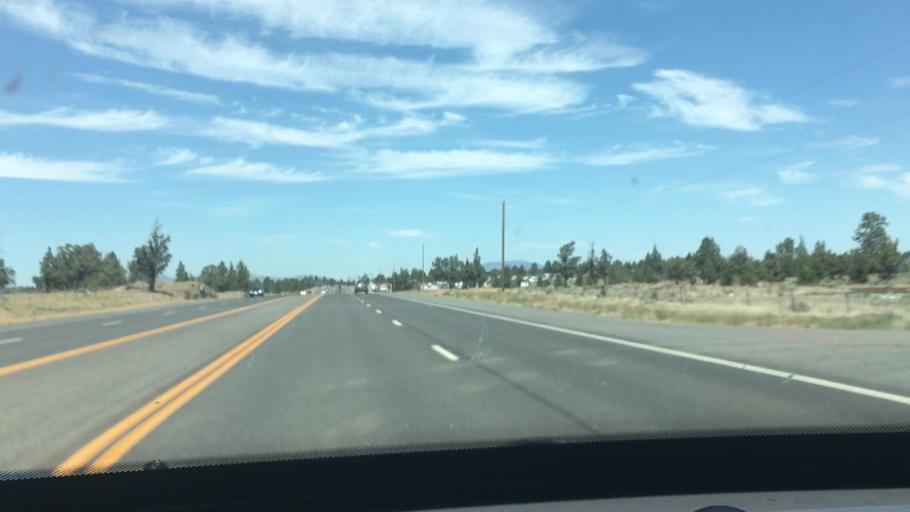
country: US
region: Oregon
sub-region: Deschutes County
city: Redmond
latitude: 44.2161
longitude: -121.2168
